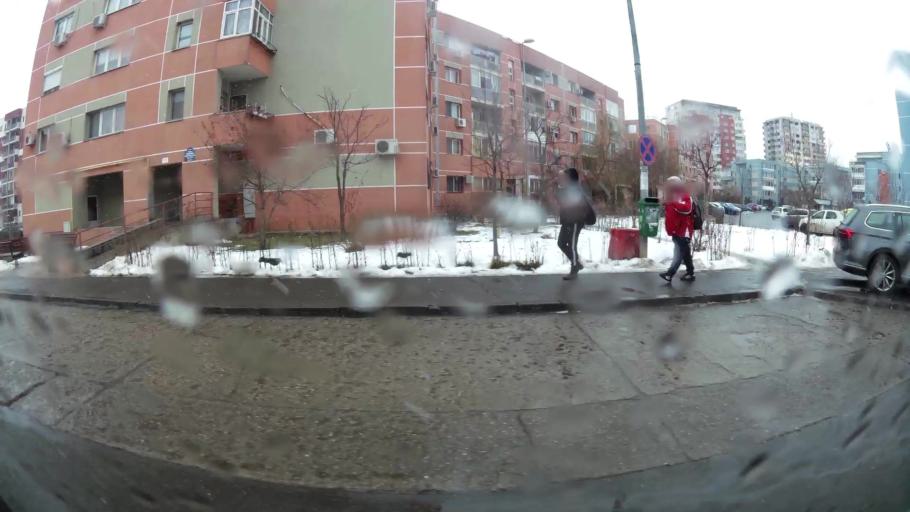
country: RO
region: Ilfov
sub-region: Comuna Chiajna
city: Rosu
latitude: 44.4190
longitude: 26.0029
